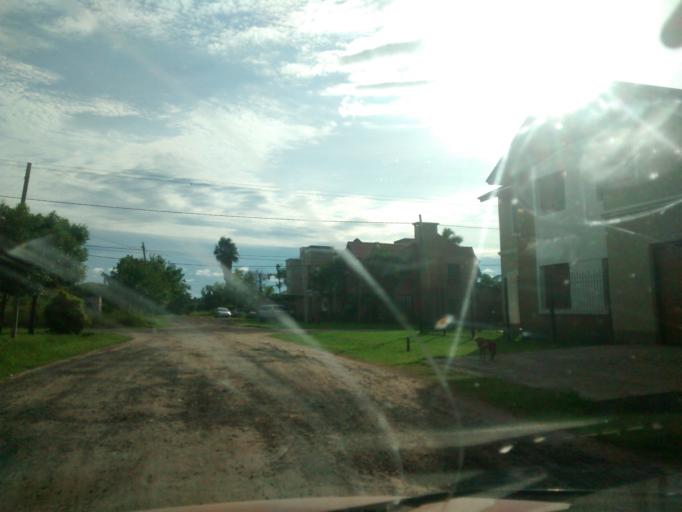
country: AR
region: Chaco
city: Resistencia
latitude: -27.4388
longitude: -58.9659
